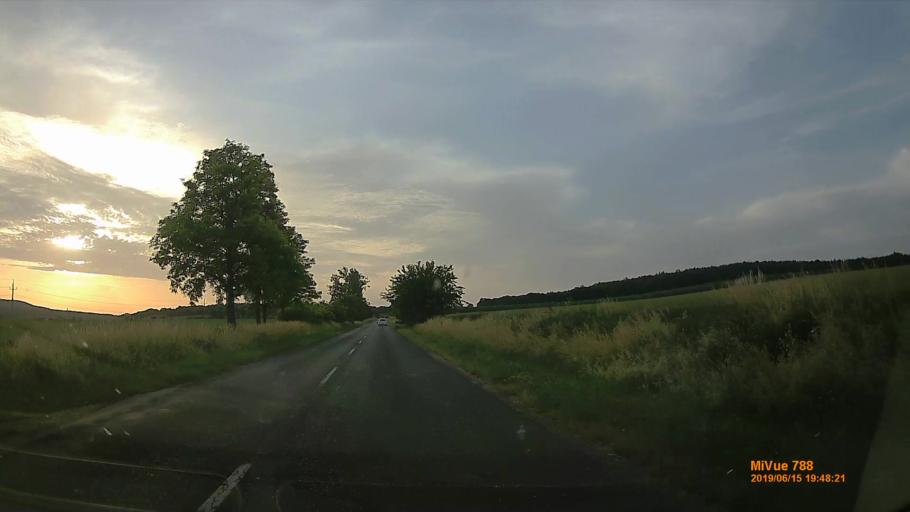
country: HU
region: Veszprem
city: Szentkiralyszabadja
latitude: 47.0233
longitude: 17.9422
